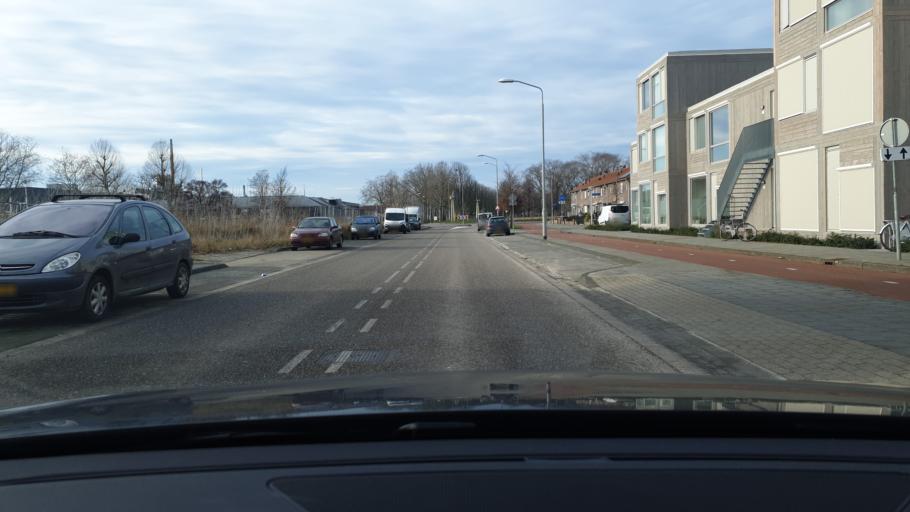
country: NL
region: North Brabant
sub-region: Gemeente Eindhoven
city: De Doornakkers
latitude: 51.4355
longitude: 5.5144
